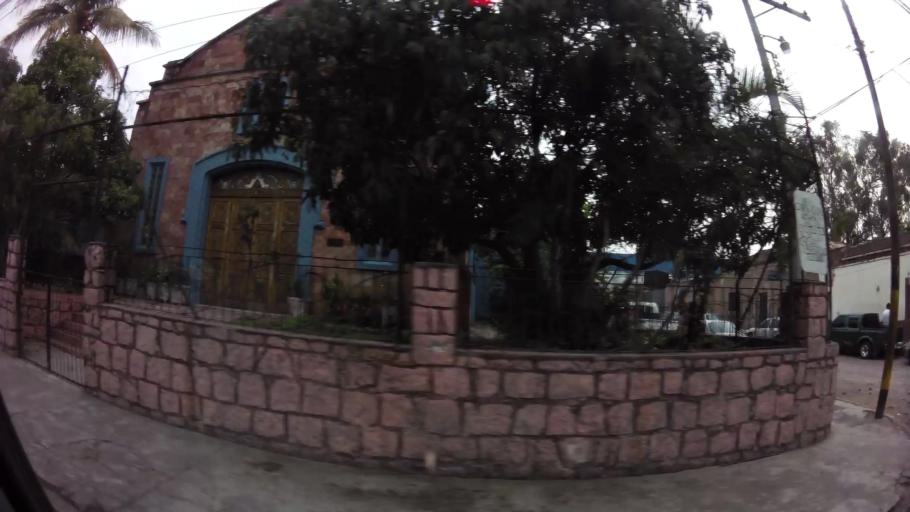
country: HN
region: Francisco Morazan
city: Tegucigalpa
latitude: 14.0899
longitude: -87.2067
